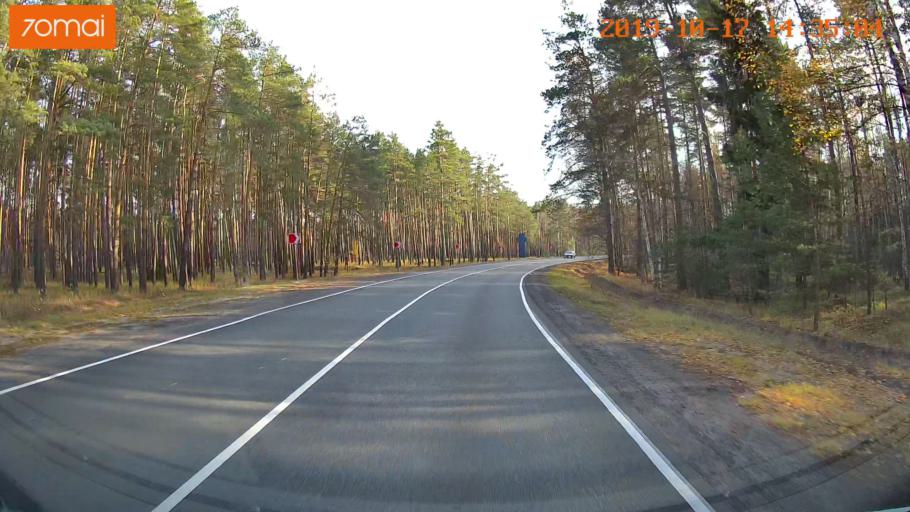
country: RU
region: Rjazan
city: Solotcha
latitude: 54.9044
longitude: 40.0026
